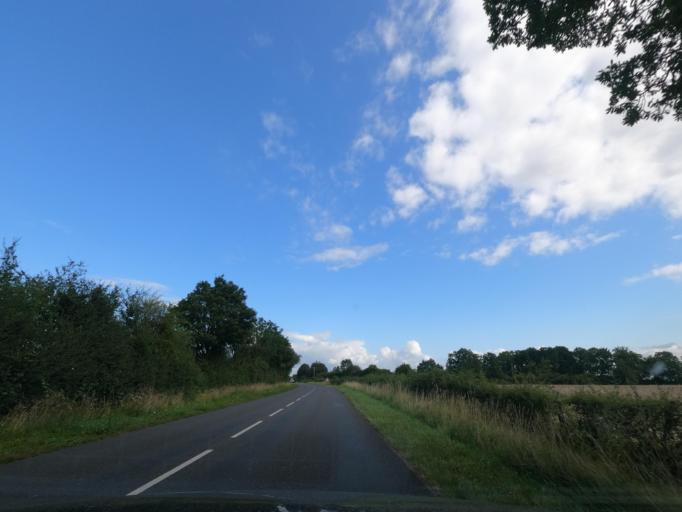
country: FR
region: Lower Normandy
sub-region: Departement de l'Orne
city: Gace
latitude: 48.7569
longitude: 0.2026
